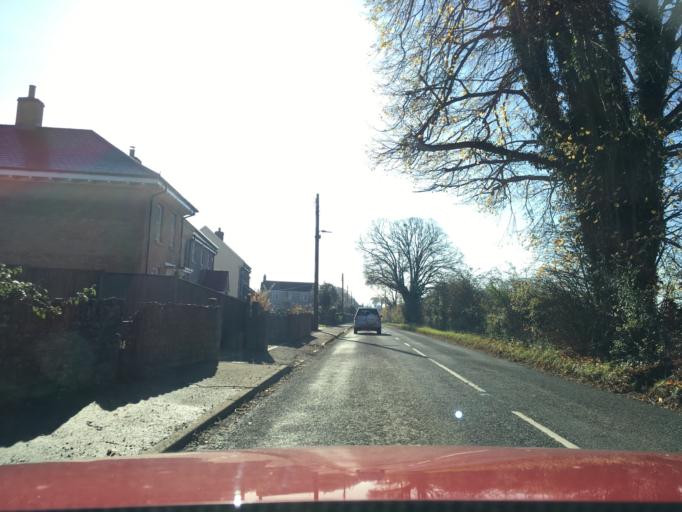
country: GB
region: England
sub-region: Somerset
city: Langport
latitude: 51.0456
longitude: -2.8248
